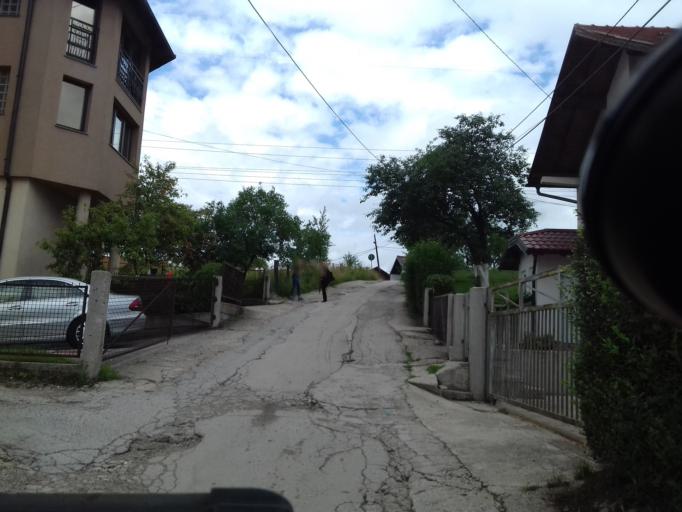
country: BA
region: Federation of Bosnia and Herzegovina
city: Zenica
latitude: 44.1991
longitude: 17.9287
